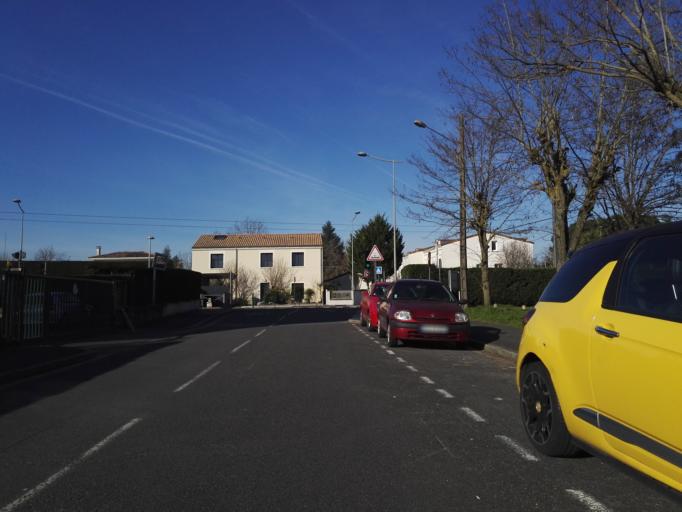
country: FR
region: Aquitaine
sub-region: Departement de la Gironde
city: Merignac
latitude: 44.8292
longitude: -0.6366
